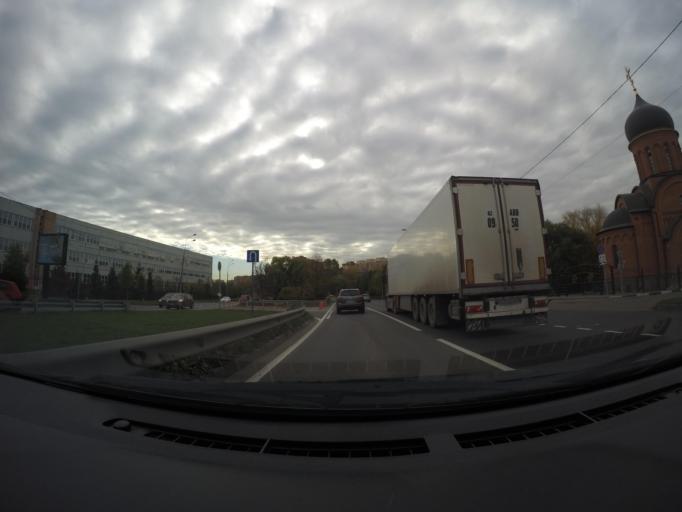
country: RU
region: Moskovskaya
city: Mytishchi
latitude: 55.9287
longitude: 37.7525
